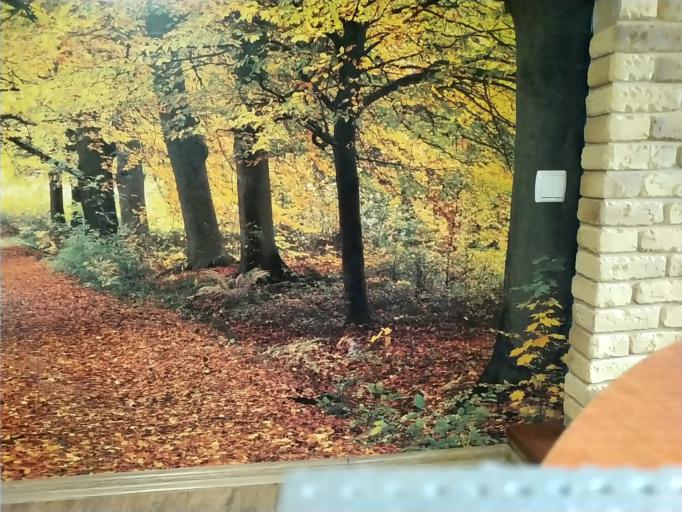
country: RU
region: Tverskaya
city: Kalashnikovo
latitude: 57.2680
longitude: 35.1677
